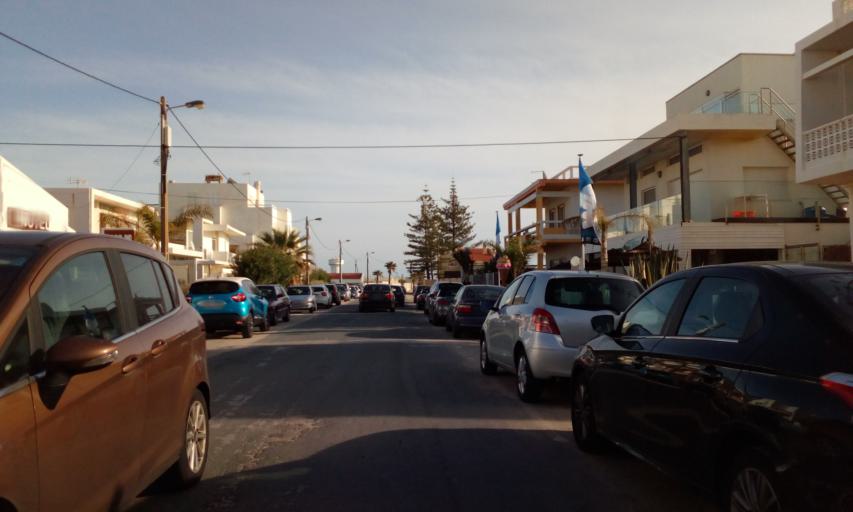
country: PT
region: Faro
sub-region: Faro
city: Faro
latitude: 37.0073
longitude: -7.9936
